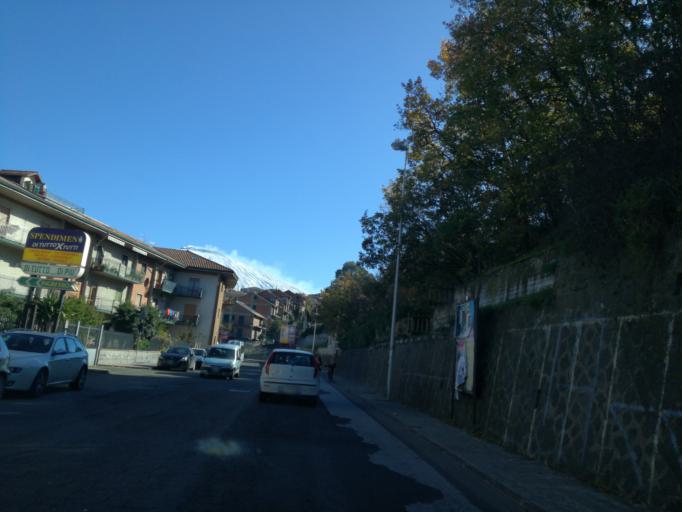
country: IT
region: Sicily
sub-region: Catania
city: Bronte
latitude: 37.7820
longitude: 14.8334
